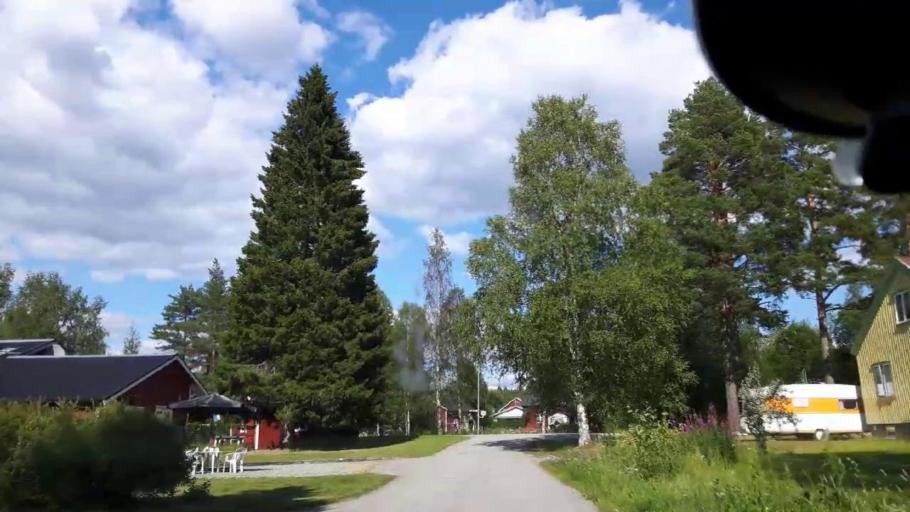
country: SE
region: Jaemtland
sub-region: Braecke Kommun
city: Braecke
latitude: 62.8317
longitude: 15.3092
